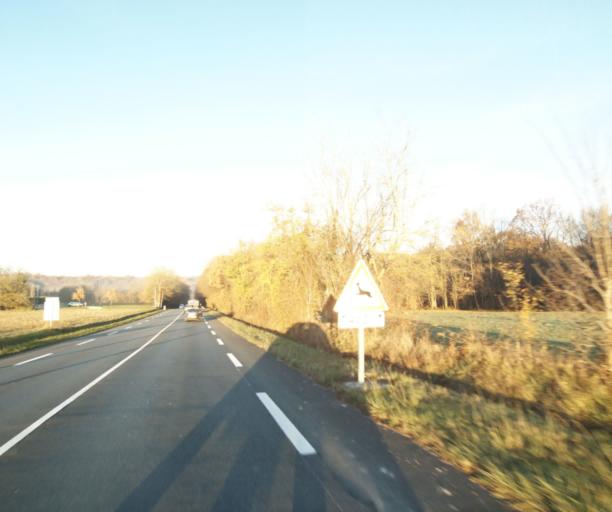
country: FR
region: Poitou-Charentes
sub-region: Departement de la Charente-Maritime
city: Chaniers
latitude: 45.7300
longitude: -0.5295
